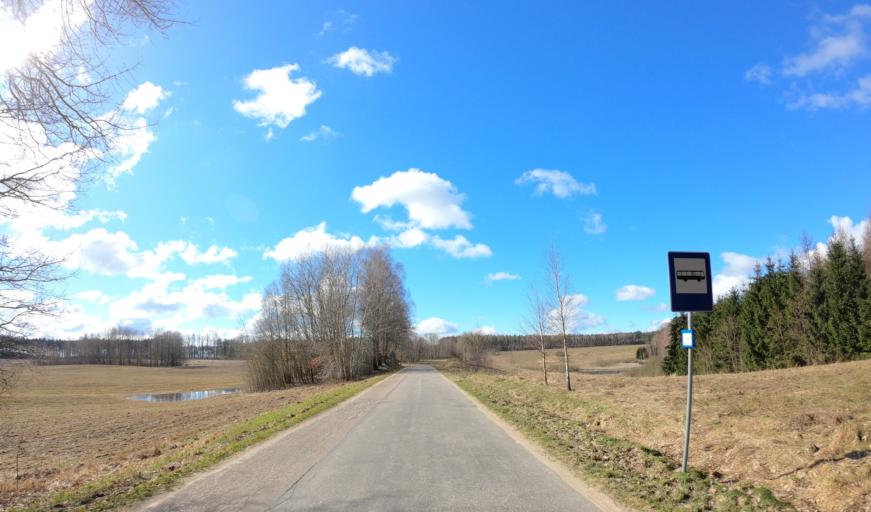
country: PL
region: West Pomeranian Voivodeship
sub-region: Powiat drawski
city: Zlocieniec
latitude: 53.4881
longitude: 15.9869
